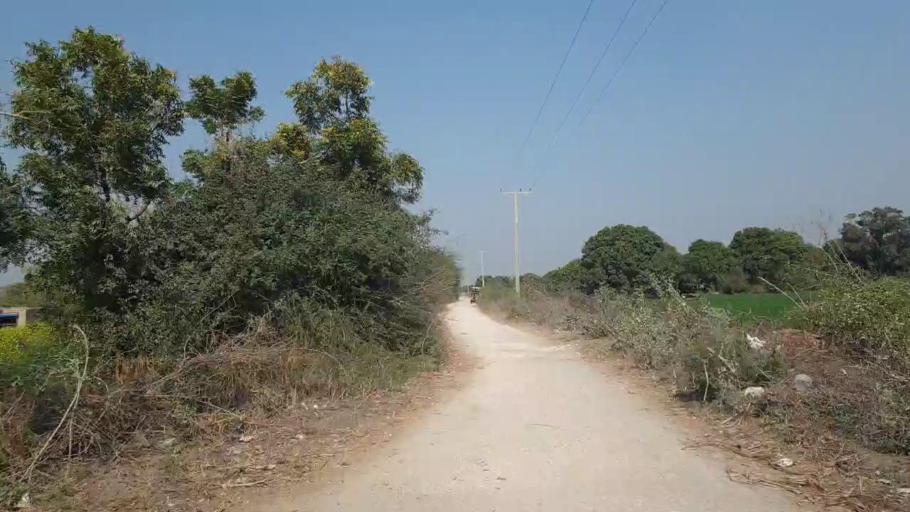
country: PK
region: Sindh
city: Chambar
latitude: 25.4051
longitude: 68.8958
